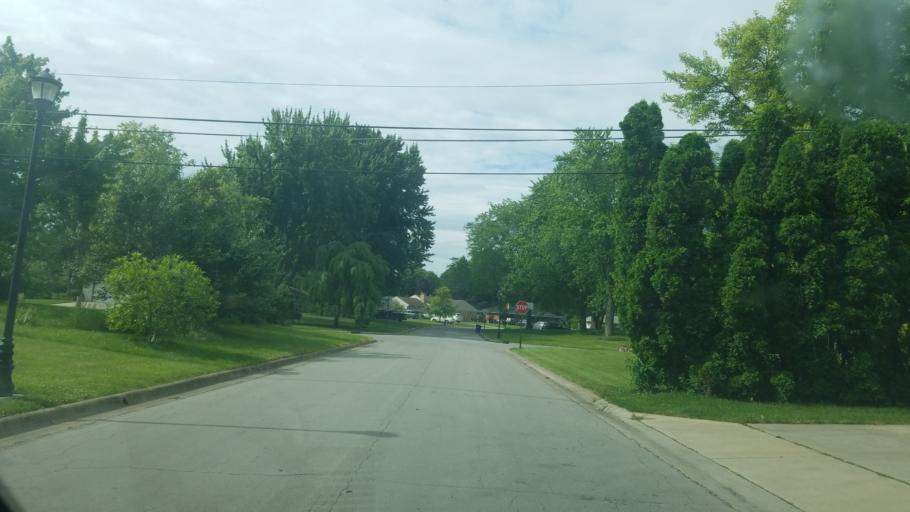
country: US
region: Ohio
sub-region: Franklin County
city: Worthington
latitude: 40.0513
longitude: -82.9908
